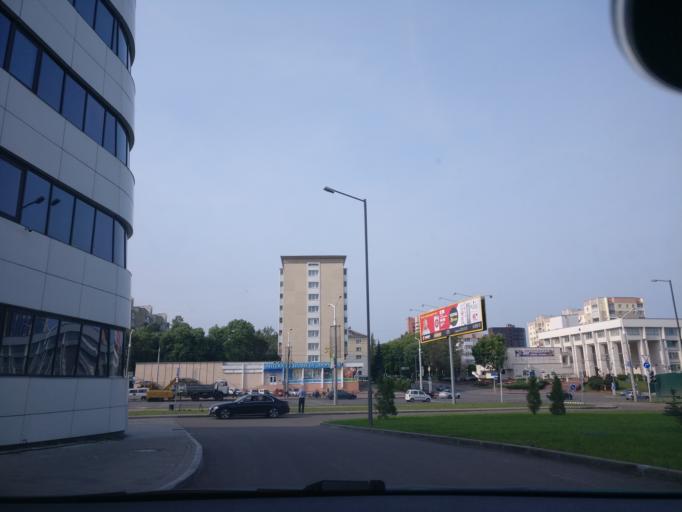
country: BY
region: Minsk
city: Minsk
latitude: 53.8926
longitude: 27.5297
